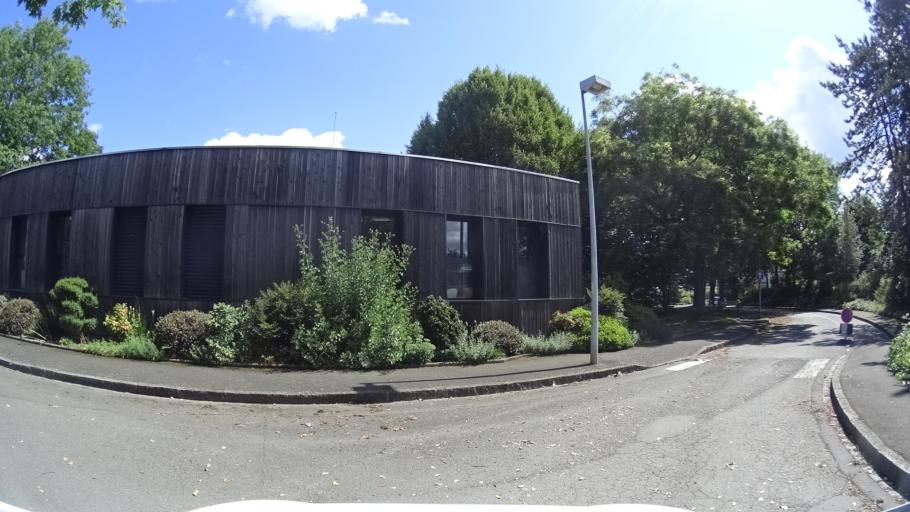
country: FR
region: Brittany
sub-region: Departement d'Ille-et-Vilaine
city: Chartres-de-Bretagne
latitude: 48.0410
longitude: -1.7074
